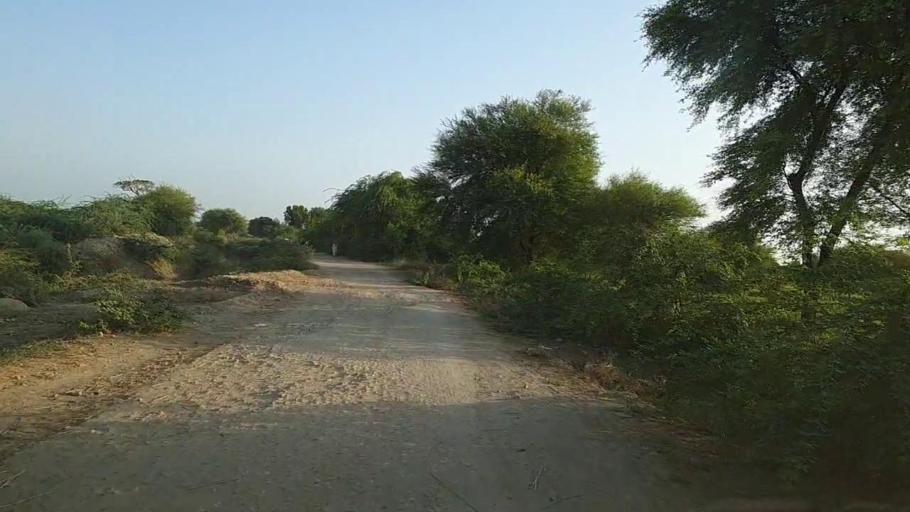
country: PK
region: Sindh
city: Kario
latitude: 24.6944
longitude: 68.6715
